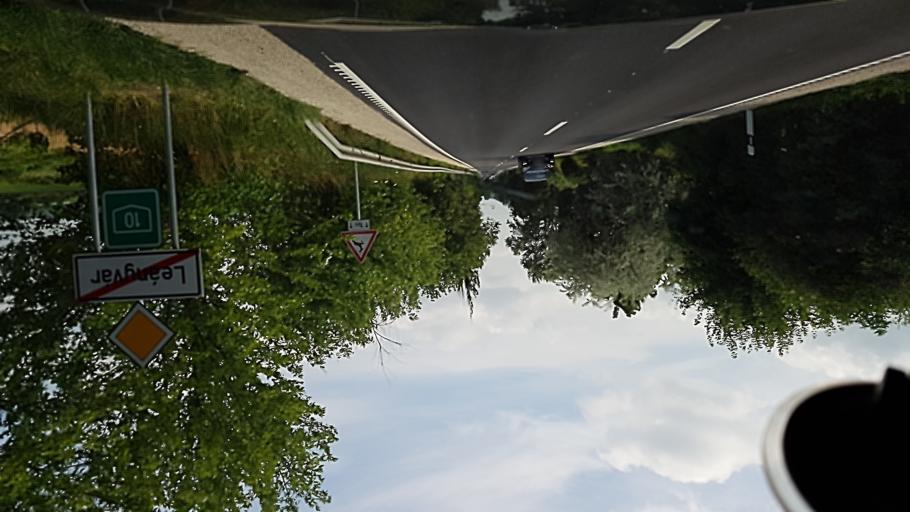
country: HU
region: Komarom-Esztergom
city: Kesztolc
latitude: 47.6910
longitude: 18.7673
